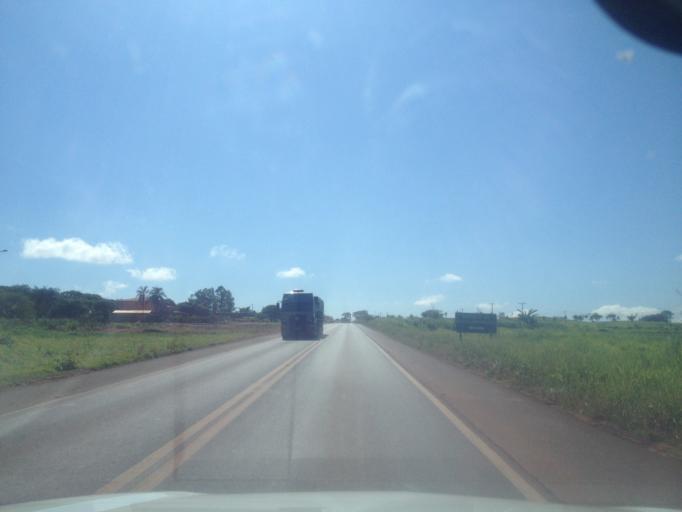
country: BR
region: Minas Gerais
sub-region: Santa Vitoria
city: Santa Vitoria
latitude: -19.0452
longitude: -50.4971
